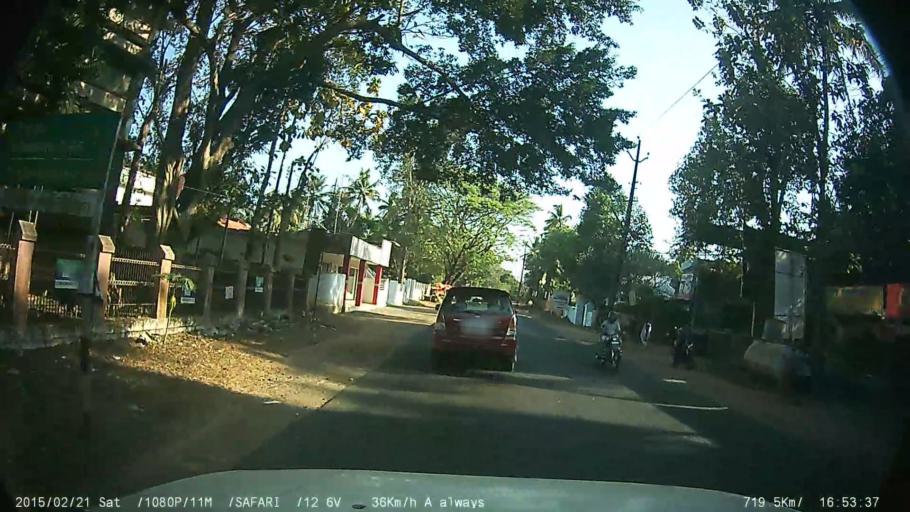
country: IN
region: Kerala
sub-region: Kottayam
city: Changanacheri
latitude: 9.4752
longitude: 76.5284
